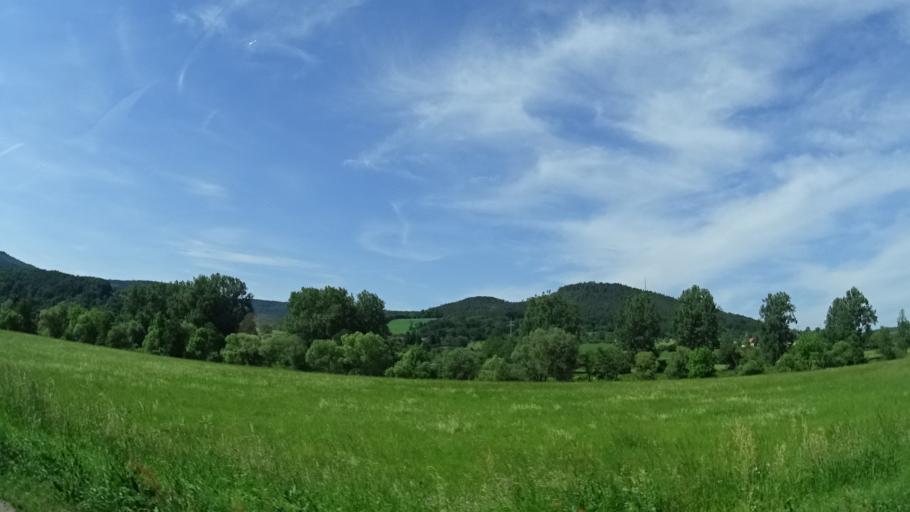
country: DE
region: Baden-Wuerttemberg
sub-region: Regierungsbezirk Stuttgart
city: Freudenberg
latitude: 49.7391
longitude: 9.3019
